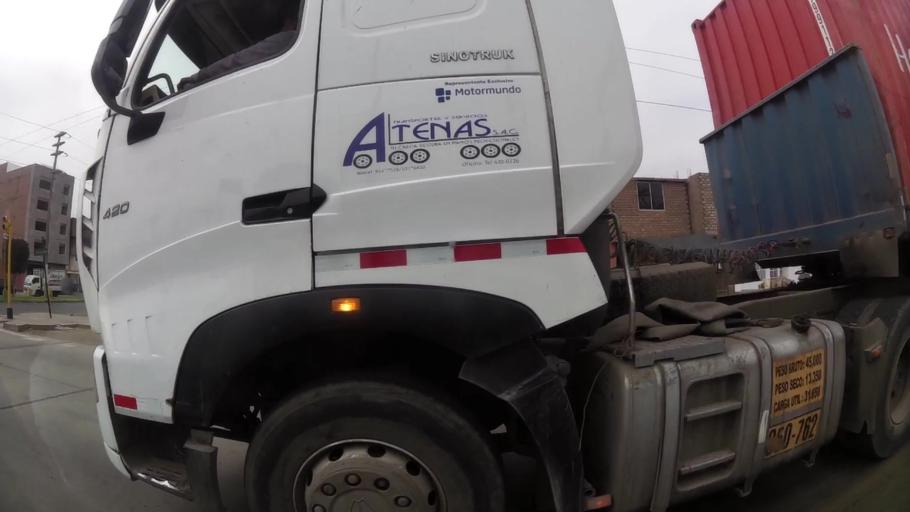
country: PE
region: Callao
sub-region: Callao
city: Callao
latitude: -12.0101
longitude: -77.1058
